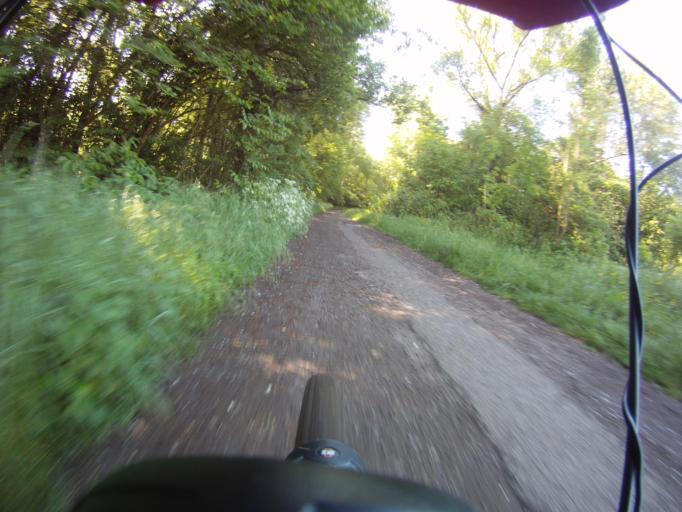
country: FR
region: Auvergne
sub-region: Departement du Puy-de-Dome
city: Dallet
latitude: 45.7633
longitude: 3.2339
